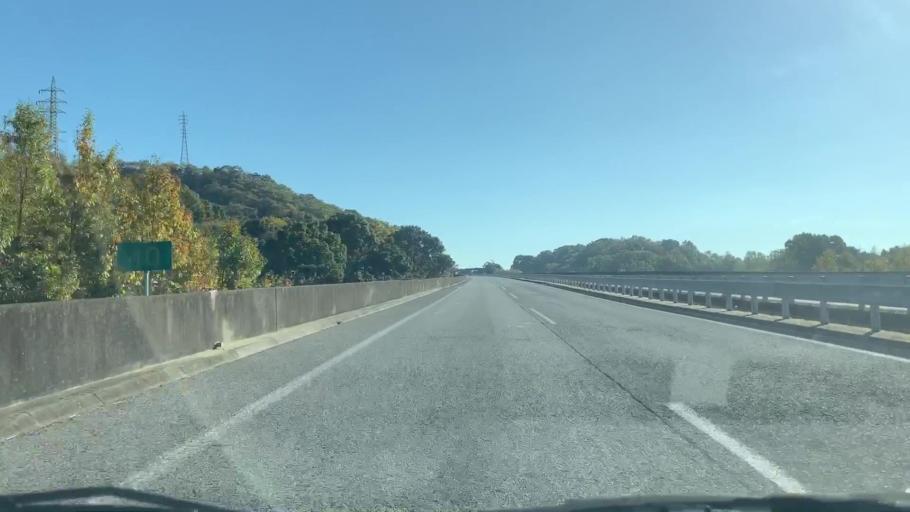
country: JP
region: Saga Prefecture
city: Saga-shi
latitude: 33.2874
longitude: 130.1475
